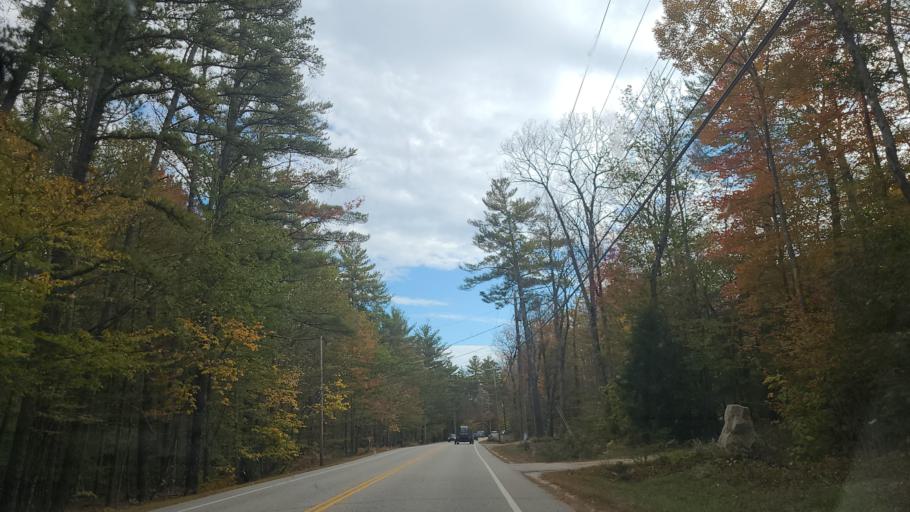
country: US
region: New Hampshire
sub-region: Carroll County
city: North Conway
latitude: 44.0384
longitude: -71.1421
